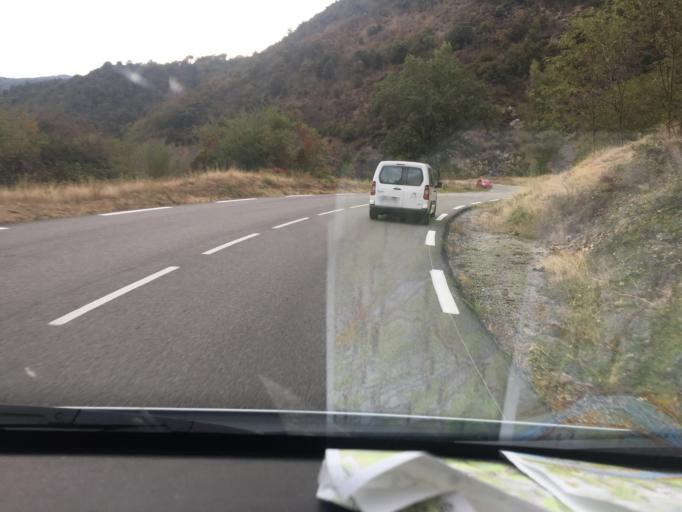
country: FR
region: Rhone-Alpes
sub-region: Departement de l'Ardeche
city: Saint-Jean-de-Muzols
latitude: 45.0610
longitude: 4.7658
